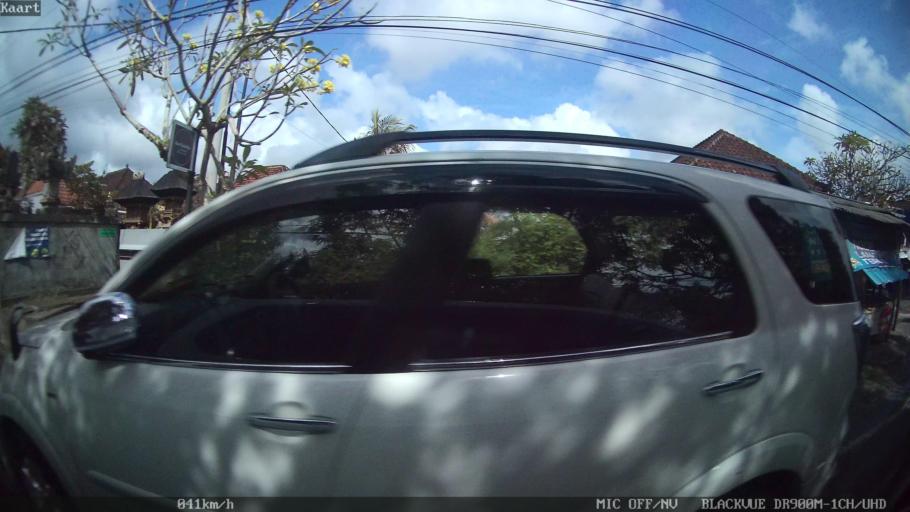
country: ID
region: Bali
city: Banjar Sedang
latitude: -8.5706
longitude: 115.2562
